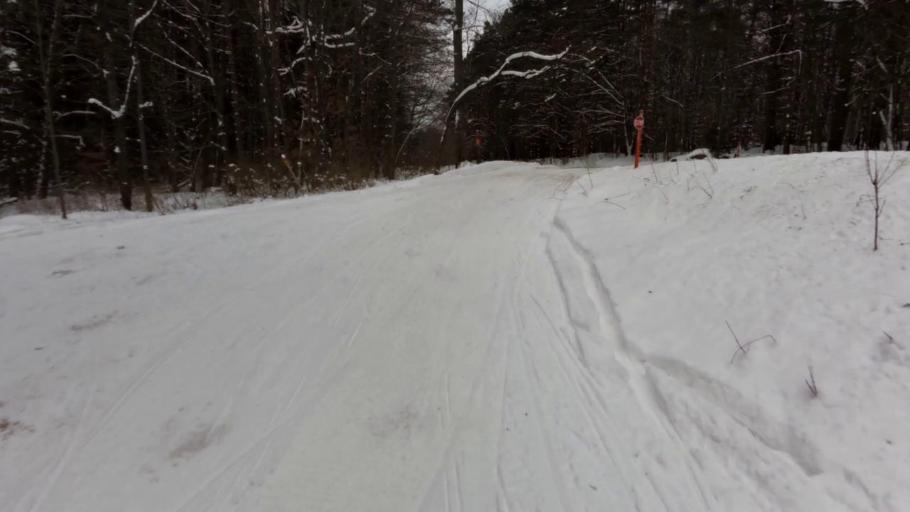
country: US
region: Pennsylvania
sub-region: McKean County
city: Bradford
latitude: 42.0280
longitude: -78.7220
